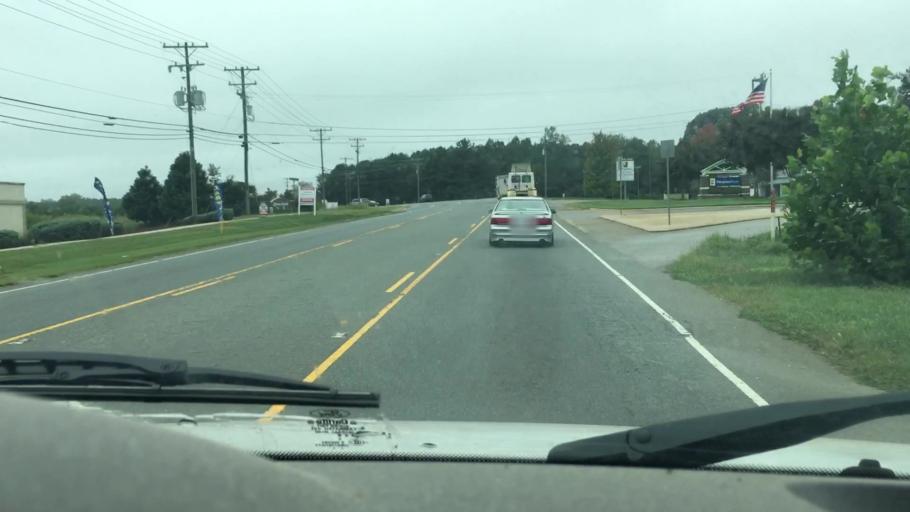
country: US
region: North Carolina
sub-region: Catawba County
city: Lake Norman of Catawba
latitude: 35.6042
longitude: -80.9035
